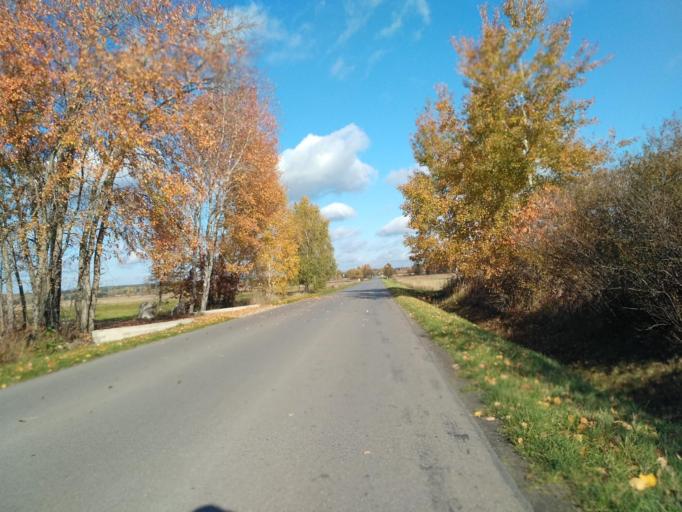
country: PL
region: Subcarpathian Voivodeship
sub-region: Powiat rzeszowski
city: Swilcza
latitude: 50.1226
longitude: 21.9008
